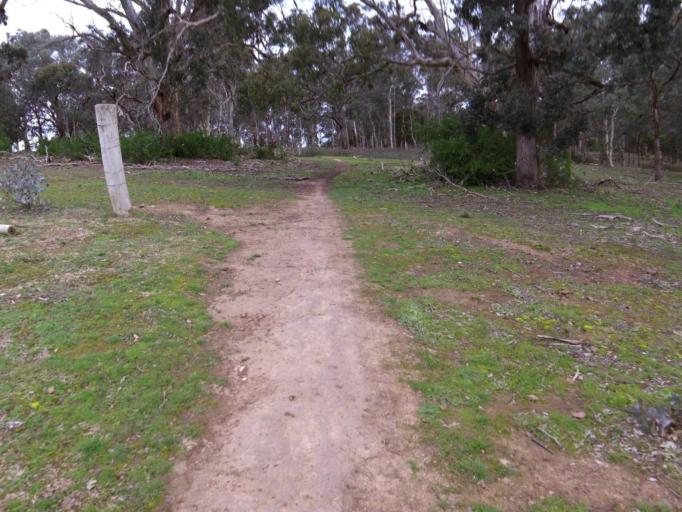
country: AU
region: Victoria
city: Plenty
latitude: -37.6728
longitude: 145.1000
